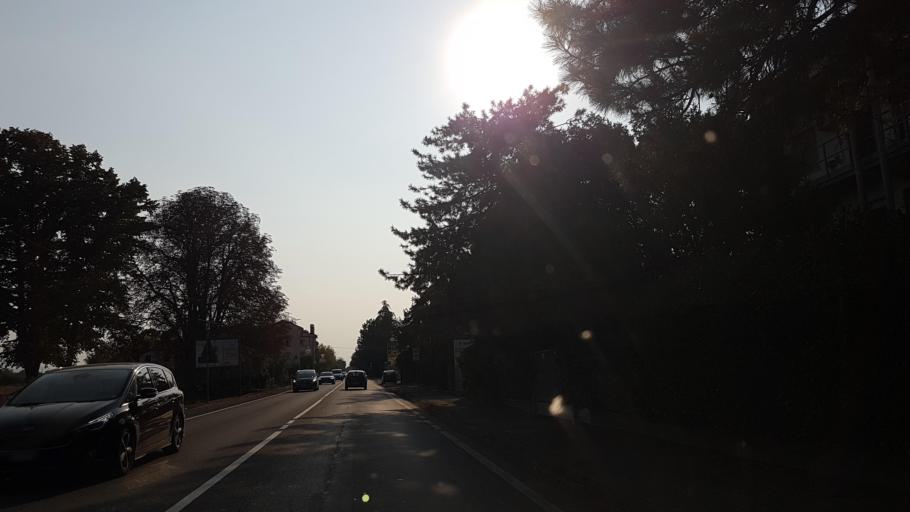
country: IT
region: Emilia-Romagna
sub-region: Provincia di Parma
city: Vicofertile
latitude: 44.7789
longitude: 10.2809
